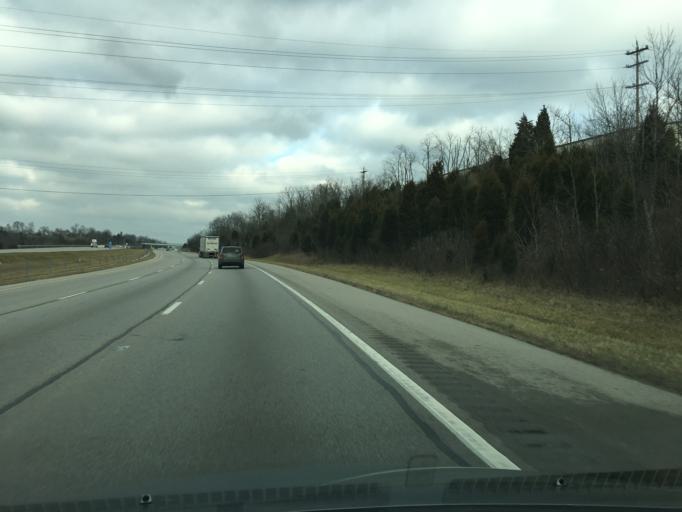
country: US
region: Ohio
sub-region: Hamilton County
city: Dry Ridge
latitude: 39.2317
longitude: -84.6310
